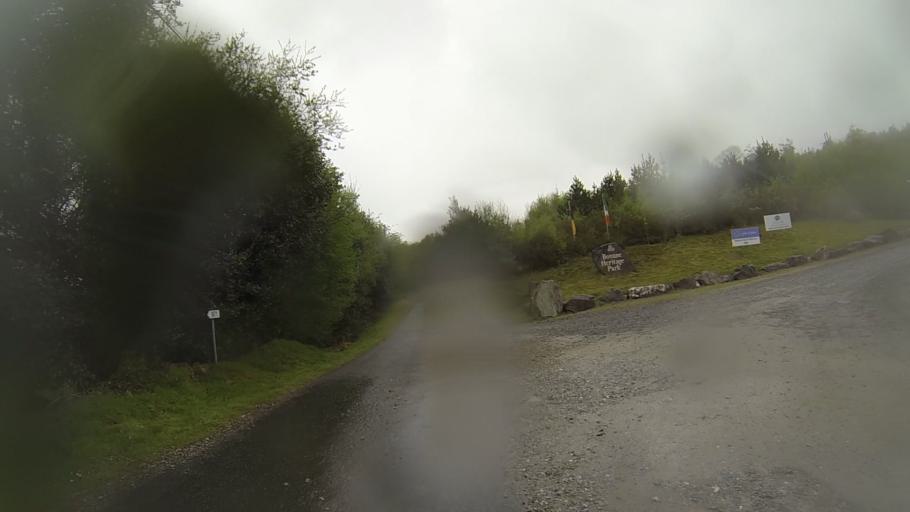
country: IE
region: Munster
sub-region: Ciarrai
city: Kenmare
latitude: 51.8295
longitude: -9.5208
